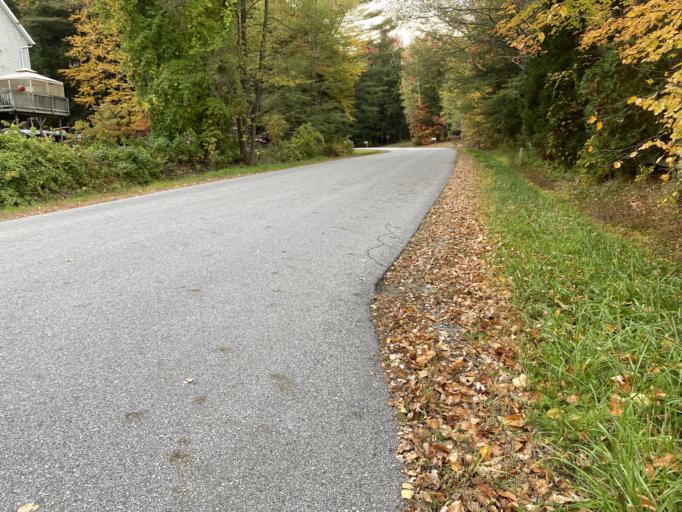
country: US
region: New York
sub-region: Saratoga County
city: Milton
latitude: 43.0964
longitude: -73.9025
